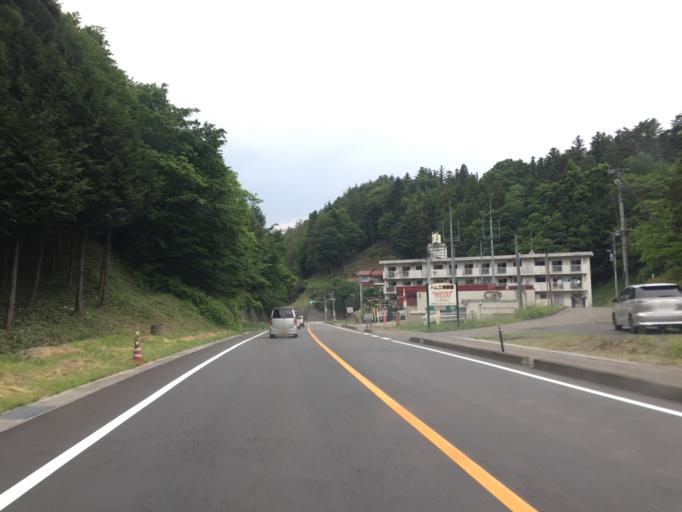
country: JP
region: Fukushima
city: Namie
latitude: 37.4336
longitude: 140.8019
